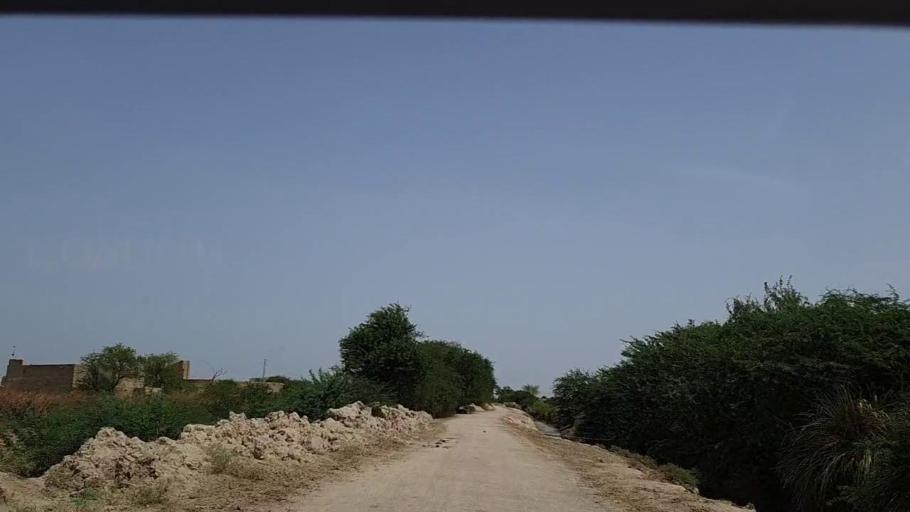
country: PK
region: Sindh
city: Johi
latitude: 26.7766
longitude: 67.6237
